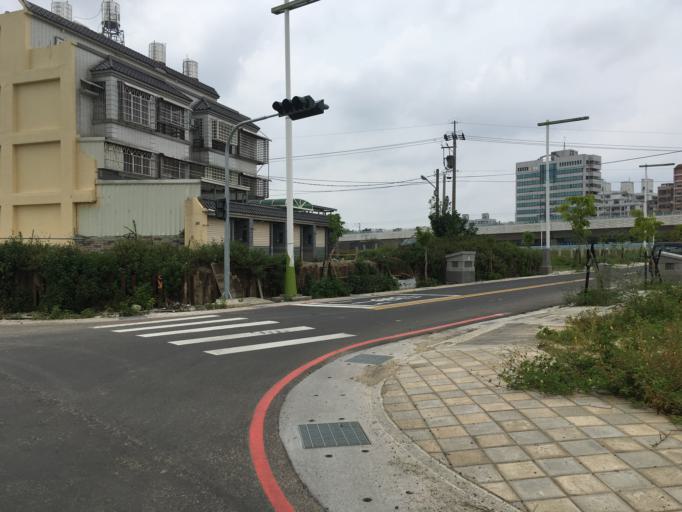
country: TW
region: Taiwan
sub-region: Taichung City
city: Taichung
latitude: 24.1839
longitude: 120.7042
